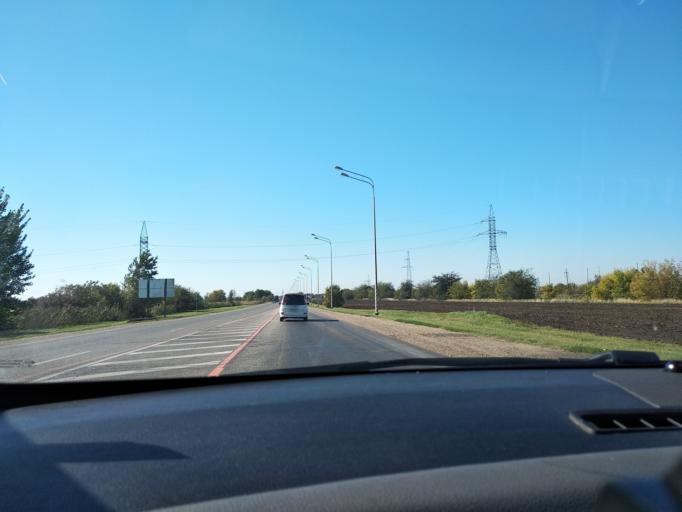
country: RU
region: Krasnodarskiy
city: Agronom
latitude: 45.1720
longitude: 39.0970
